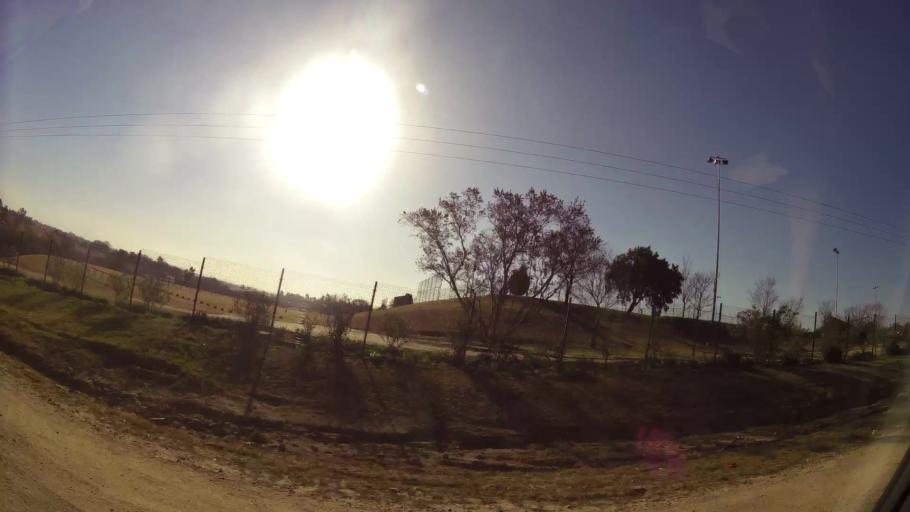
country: ZA
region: Gauteng
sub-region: City of Johannesburg Metropolitan Municipality
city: Diepsloot
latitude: -25.9526
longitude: 27.9630
